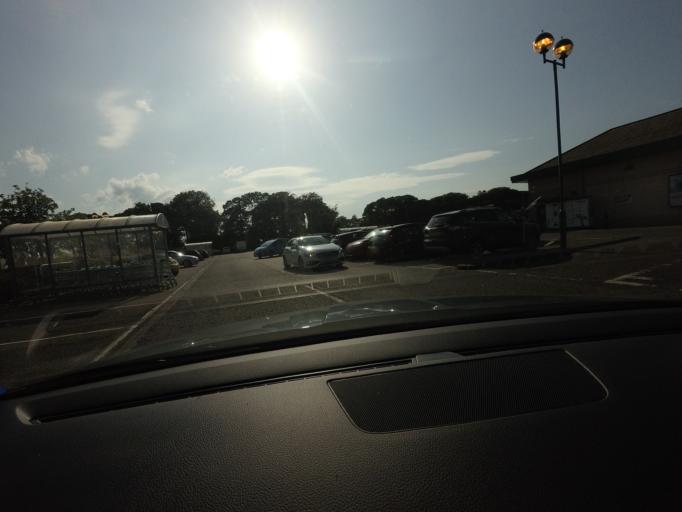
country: GB
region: Scotland
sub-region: Highland
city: Alness
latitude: 57.6929
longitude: -4.2422
